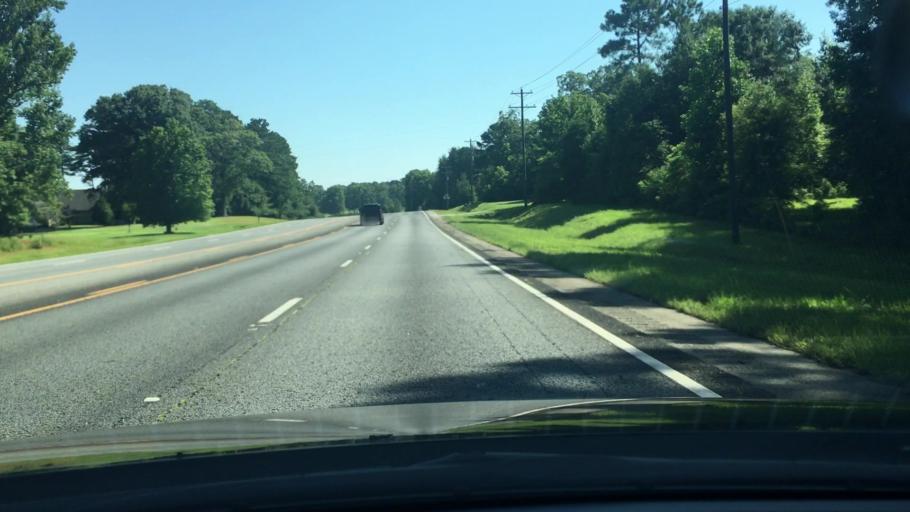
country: US
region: Georgia
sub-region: Pike County
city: Zebulon
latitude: 33.1480
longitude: -84.3148
